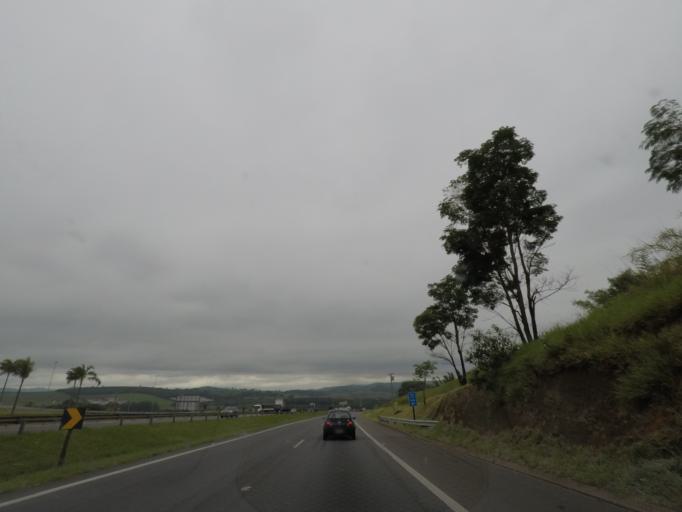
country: BR
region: Sao Paulo
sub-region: Jarinu
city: Jarinu
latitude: -23.0377
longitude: -46.6883
